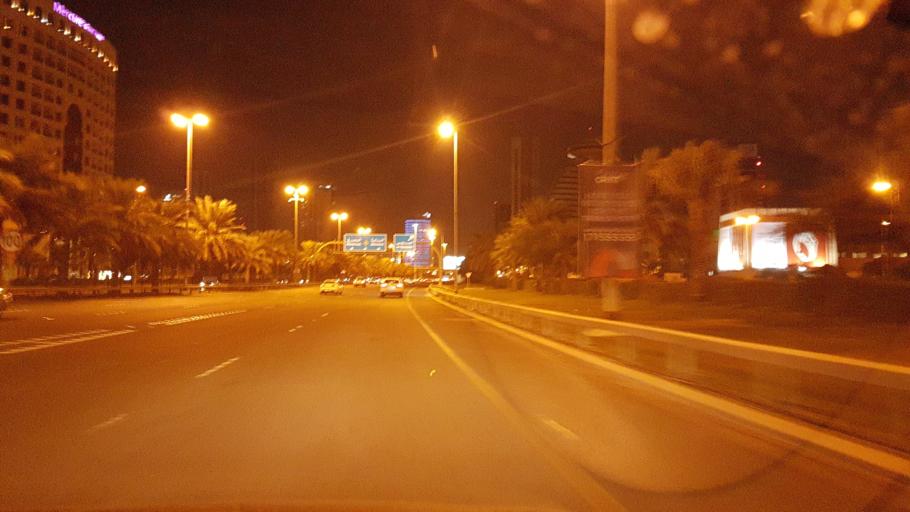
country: BH
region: Manama
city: Jidd Hafs
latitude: 26.2312
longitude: 50.5395
